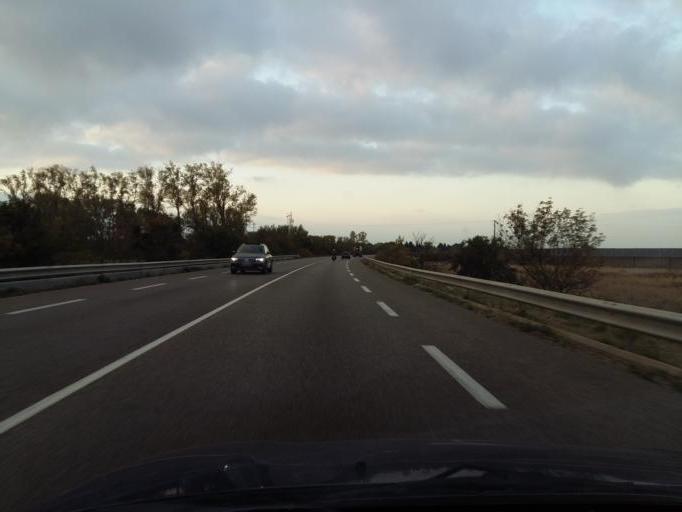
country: FR
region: Provence-Alpes-Cote d'Azur
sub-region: Departement des Bouches-du-Rhone
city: Miramas
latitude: 43.5752
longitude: 4.9841
